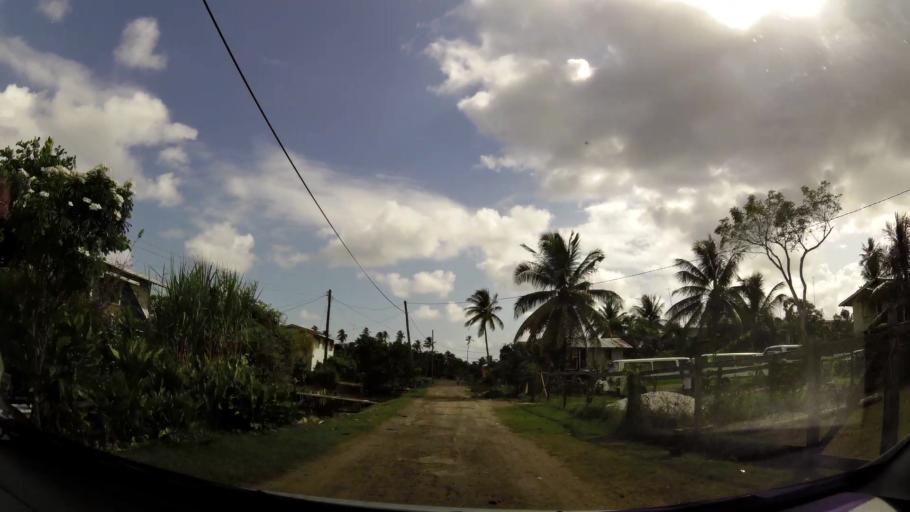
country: GY
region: Demerara-Mahaica
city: Mahaica Village
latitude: 6.6684
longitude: -57.9267
